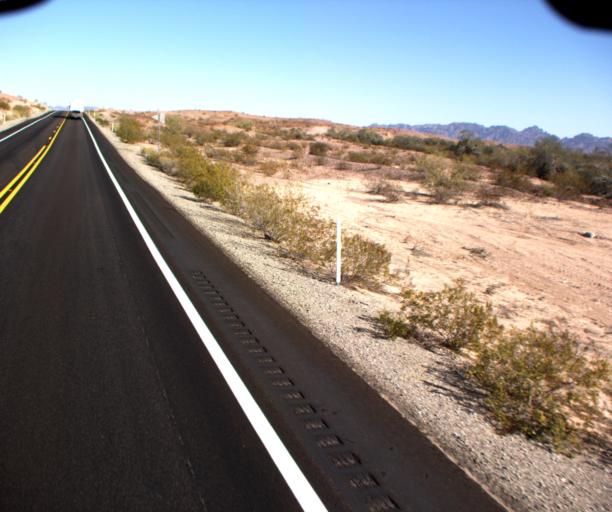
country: US
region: Arizona
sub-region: Yuma County
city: Wellton
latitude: 33.0723
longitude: -114.2944
